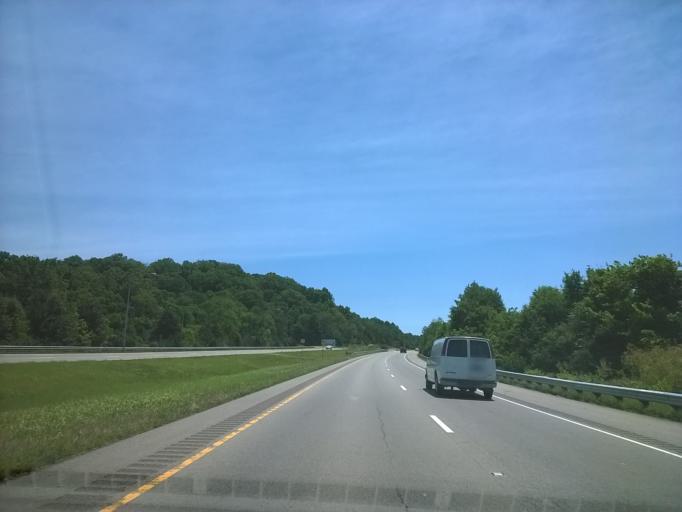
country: US
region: Ohio
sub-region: Hamilton County
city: Harrison
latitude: 39.2787
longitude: -84.8271
